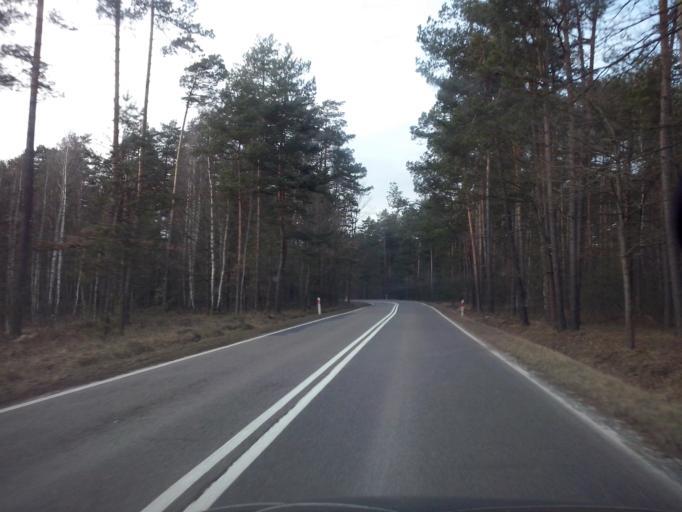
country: PL
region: Lublin Voivodeship
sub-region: Powiat bilgorajski
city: Biszcza
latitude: 50.5023
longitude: 22.6007
